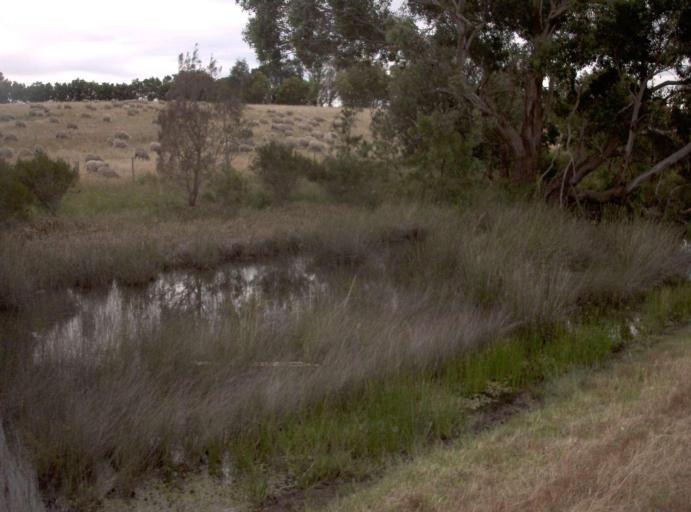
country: AU
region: Victoria
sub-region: East Gippsland
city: Bairnsdale
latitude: -37.9901
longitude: 147.3965
